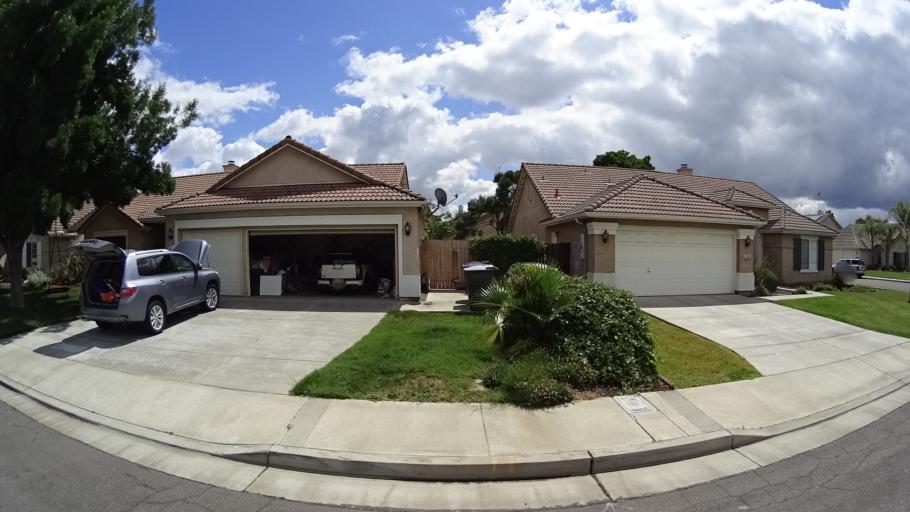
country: US
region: California
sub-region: Kings County
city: Lucerne
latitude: 36.3611
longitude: -119.6590
